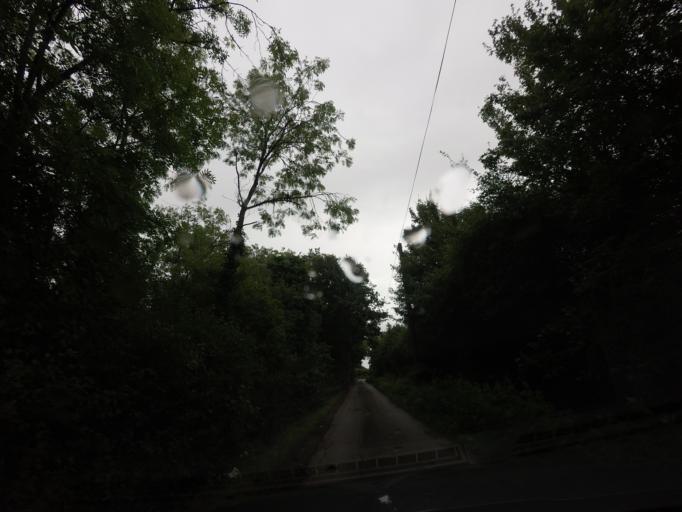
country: GB
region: England
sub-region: Kent
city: Paddock Wood
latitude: 51.1892
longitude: 0.4167
